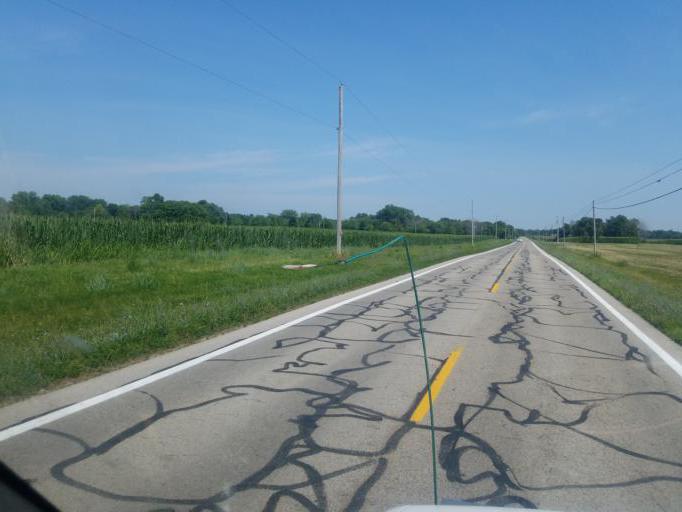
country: US
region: Ohio
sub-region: Mercer County
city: Celina
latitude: 40.4957
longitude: -84.5639
